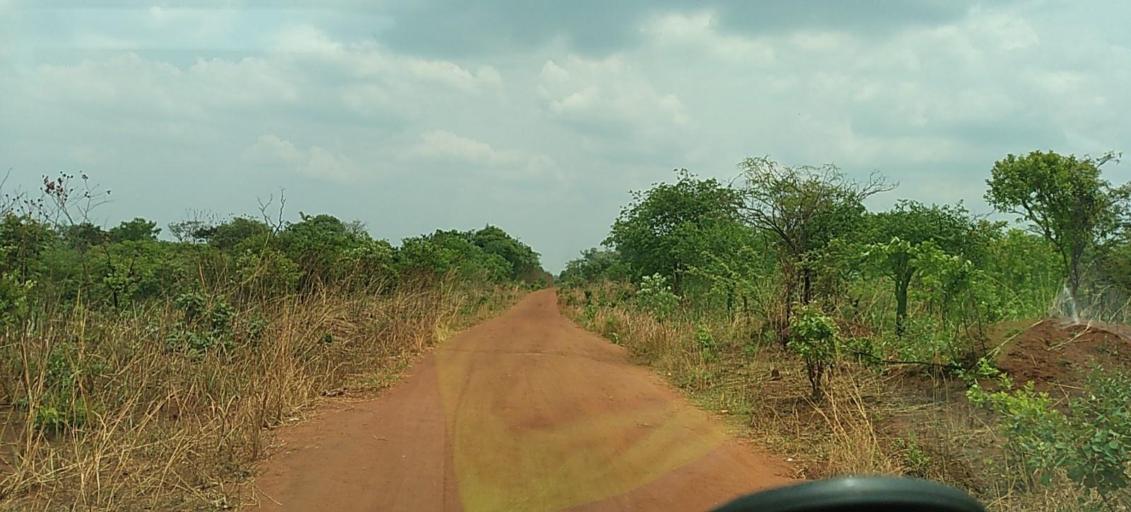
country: ZM
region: North-Western
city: Kansanshi
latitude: -12.0434
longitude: 26.3870
